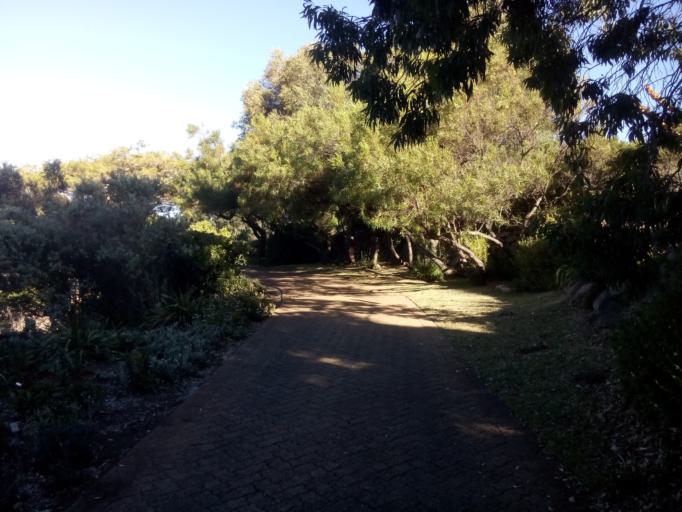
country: ZA
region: Western Cape
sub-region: City of Cape Town
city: Newlands
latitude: -33.9896
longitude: 18.4285
